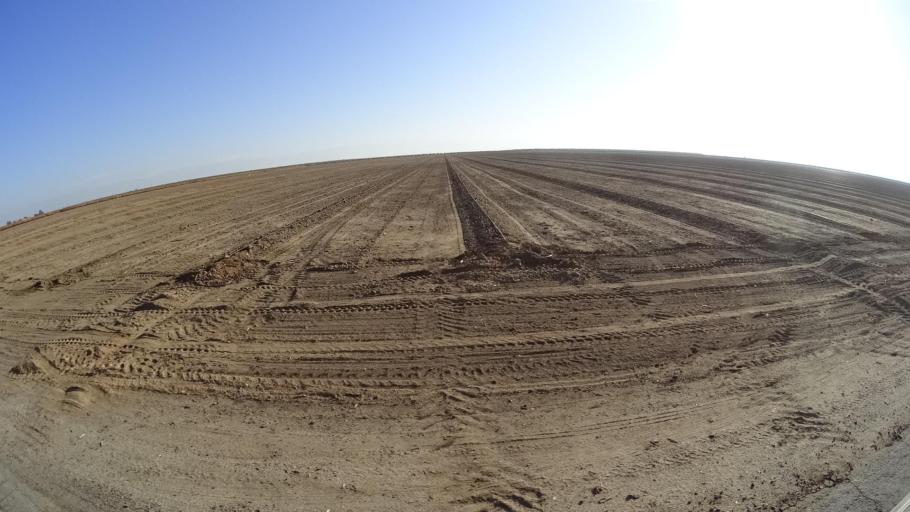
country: US
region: California
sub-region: Tulare County
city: Richgrove
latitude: 35.7664
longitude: -119.1518
